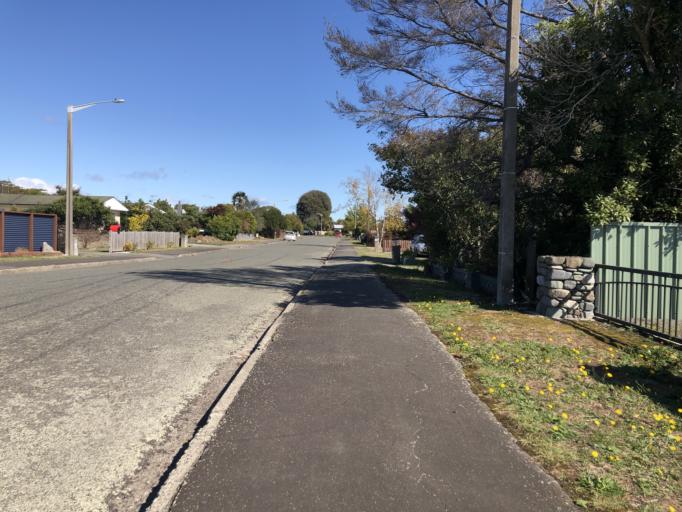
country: NZ
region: Tasman
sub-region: Tasman District
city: Richmond
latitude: -41.3411
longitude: 173.1765
